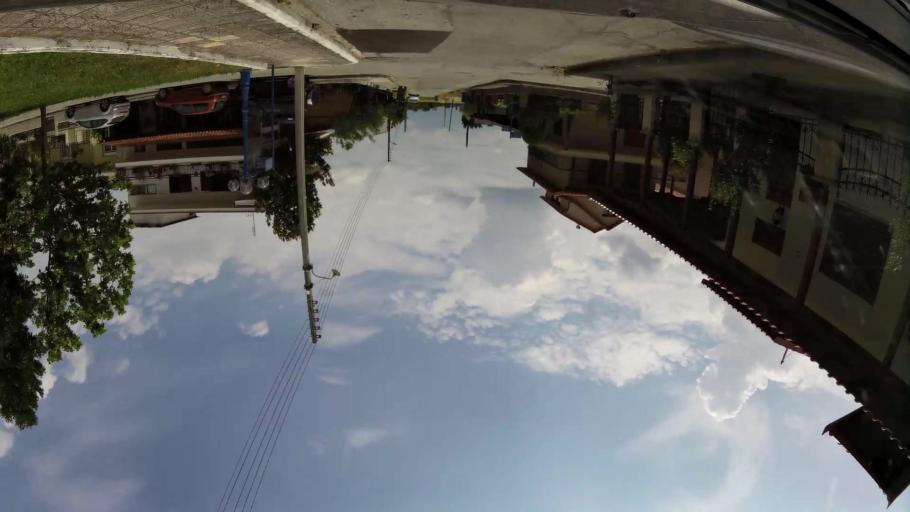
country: GR
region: Central Macedonia
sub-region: Nomos Pierias
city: Kallithea
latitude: 40.2681
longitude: 22.5810
